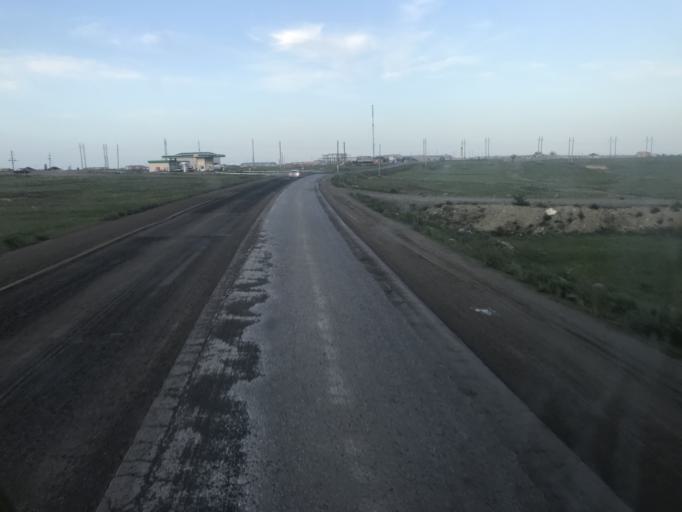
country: KZ
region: Aqtoebe
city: Khromtau
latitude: 50.2594
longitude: 58.4031
